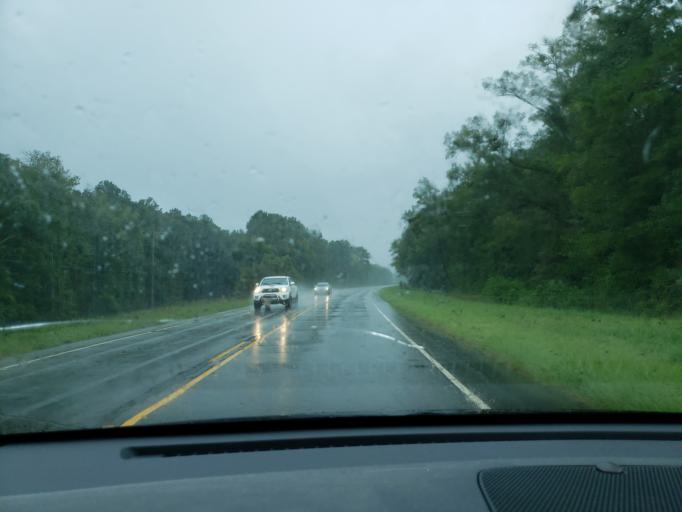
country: US
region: North Carolina
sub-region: Bladen County
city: Elizabethtown
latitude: 34.5235
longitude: -78.6507
